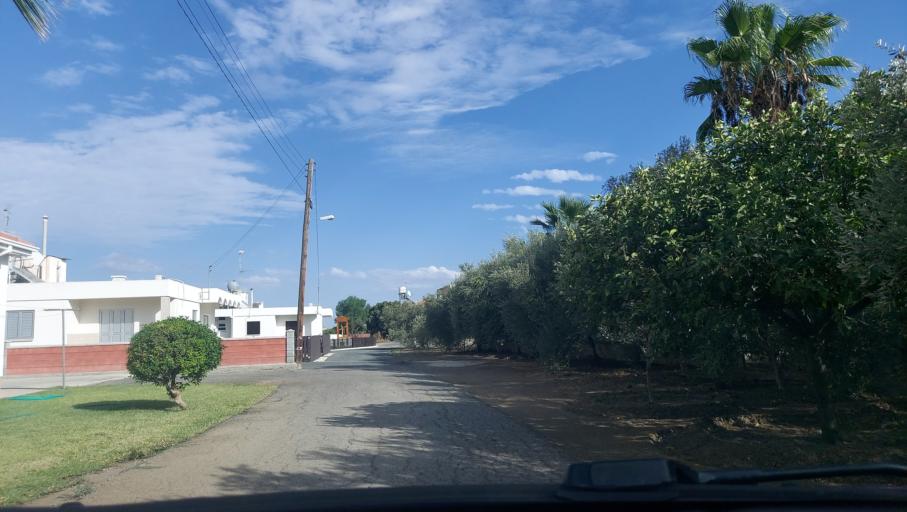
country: CY
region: Lefkosia
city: Pano Deftera
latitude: 35.0848
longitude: 33.2648
